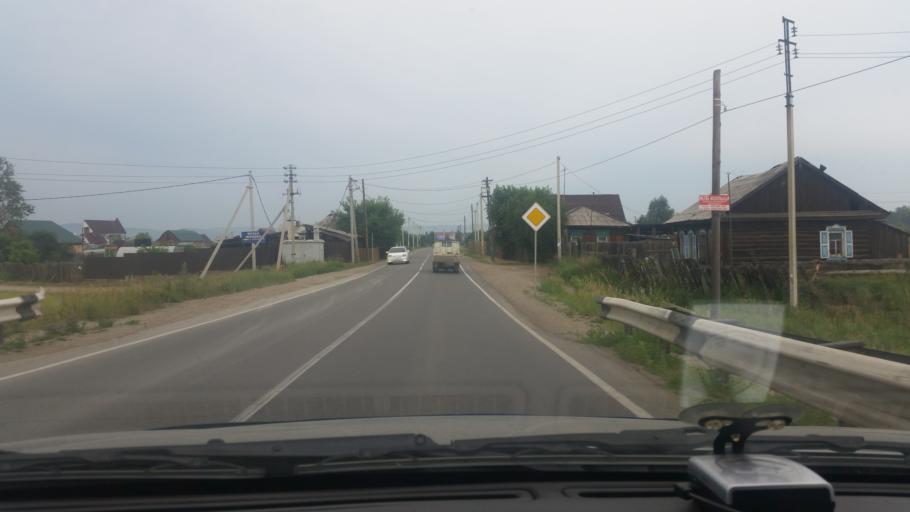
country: RU
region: Irkutsk
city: Baklashi
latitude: 52.2261
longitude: 104.0379
